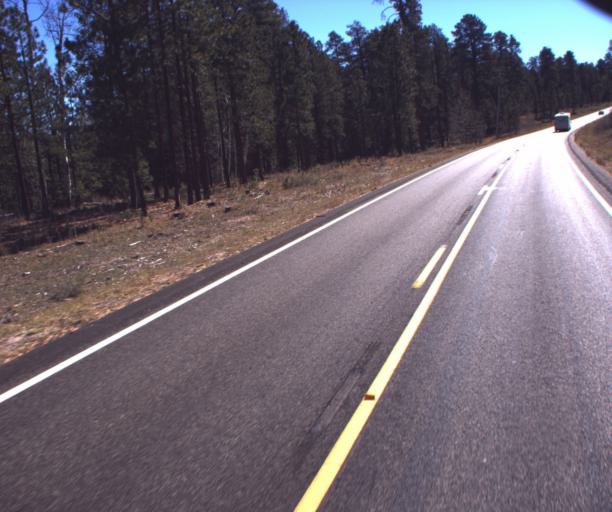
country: US
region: Arizona
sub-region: Coconino County
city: Fredonia
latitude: 36.6522
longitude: -112.1844
